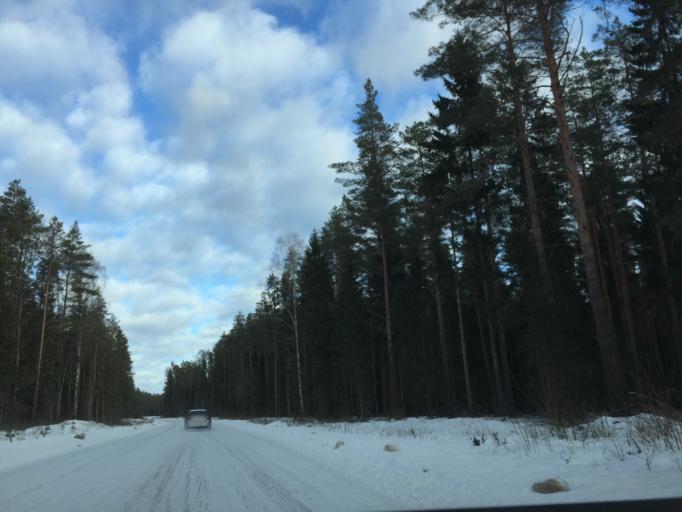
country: LV
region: Ogre
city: Jumprava
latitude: 56.5532
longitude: 24.8982
